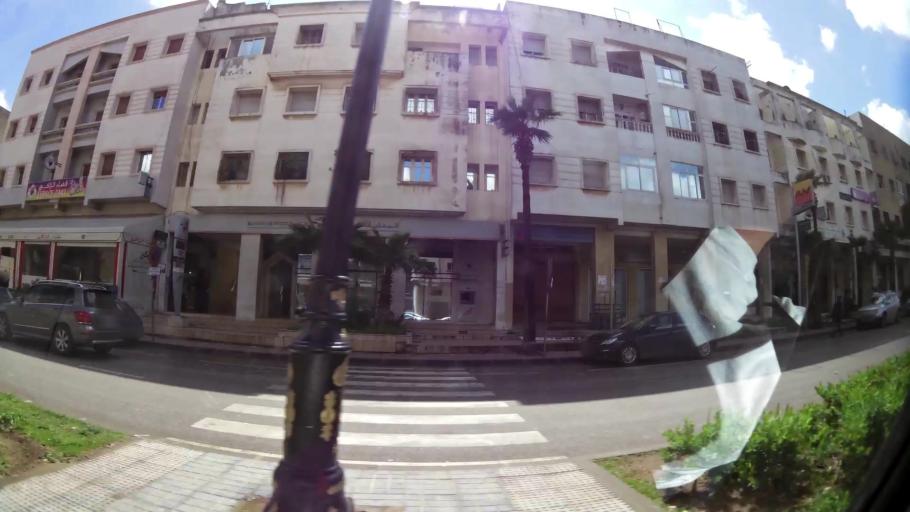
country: MA
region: Grand Casablanca
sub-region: Mediouna
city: Tit Mellil
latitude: 33.5525
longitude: -7.4826
